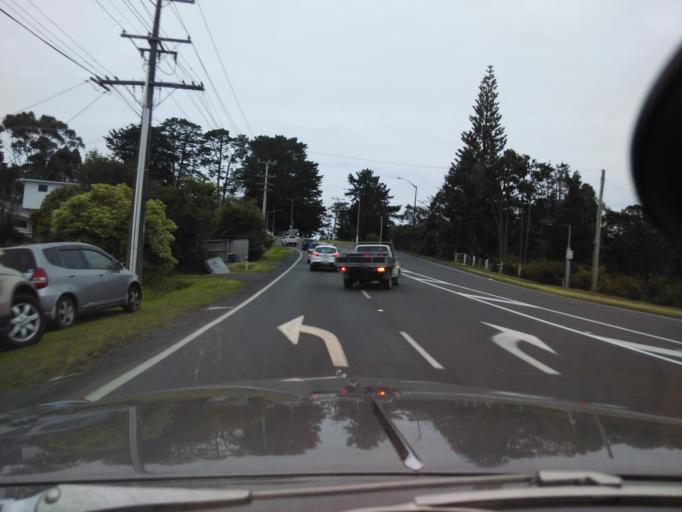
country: NZ
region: Auckland
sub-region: Auckland
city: Rothesay Bay
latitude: -36.7591
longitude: 174.7057
